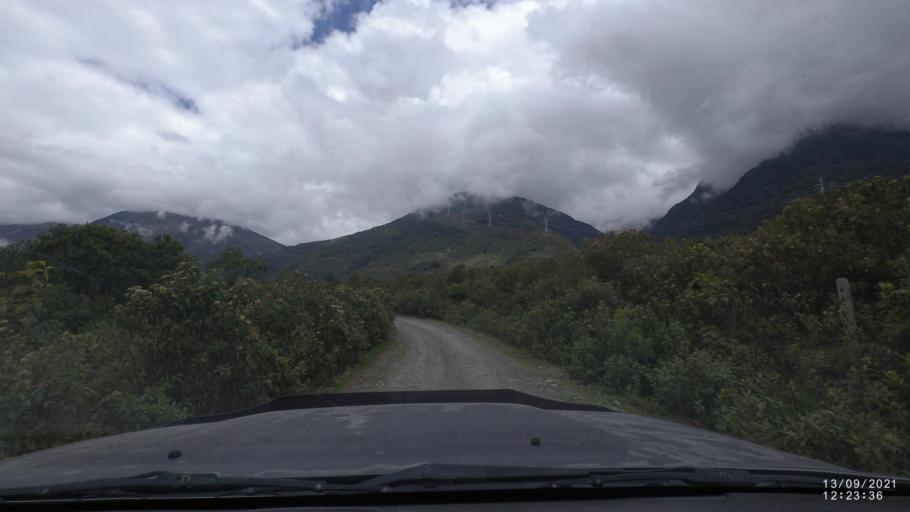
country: BO
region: Cochabamba
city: Colomi
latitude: -17.2430
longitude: -65.8184
